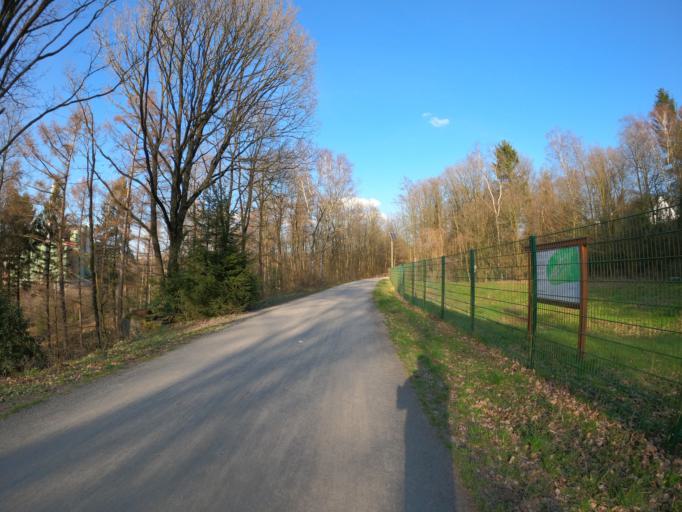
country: DE
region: North Rhine-Westphalia
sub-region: Regierungsbezirk Dusseldorf
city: Wuppertal
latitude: 51.2215
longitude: 7.1430
